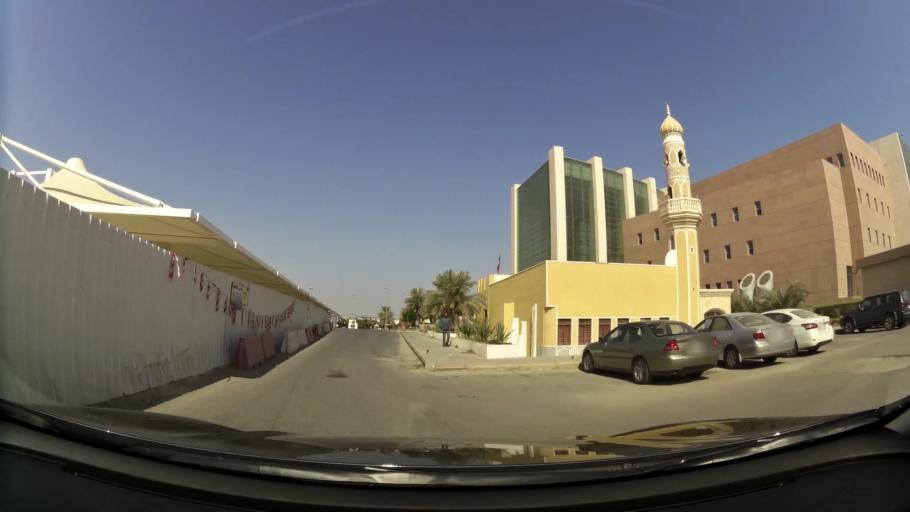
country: KW
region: Al Asimah
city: Kuwait City
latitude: 29.3738
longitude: 47.9685
